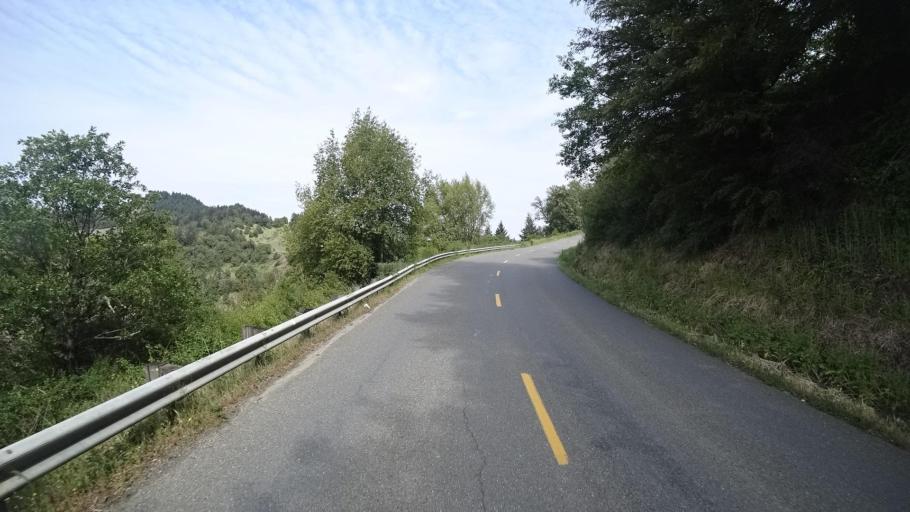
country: US
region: California
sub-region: Humboldt County
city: Redway
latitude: 40.0969
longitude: -123.7988
